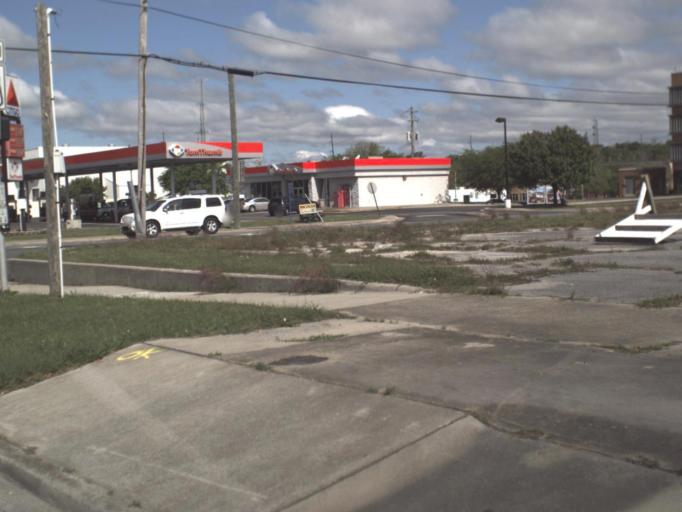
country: US
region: Florida
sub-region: Escambia County
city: Pensacola
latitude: 30.4119
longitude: -87.2414
